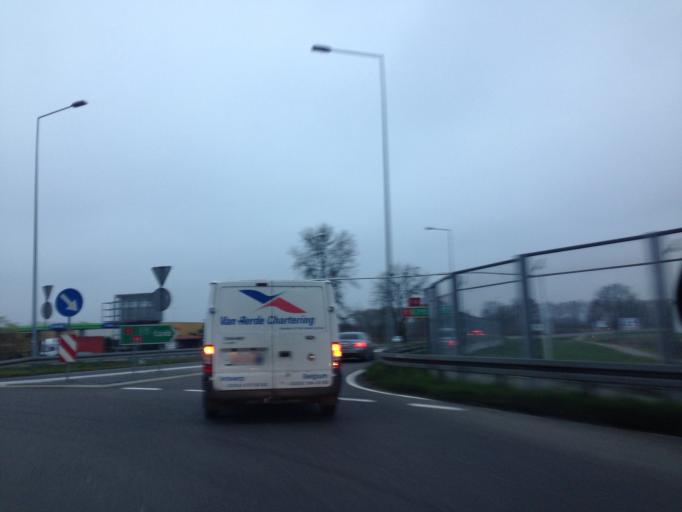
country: PL
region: Lodz Voivodeship
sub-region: Powiat zgierski
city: Strykow
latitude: 51.8829
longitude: 19.5824
